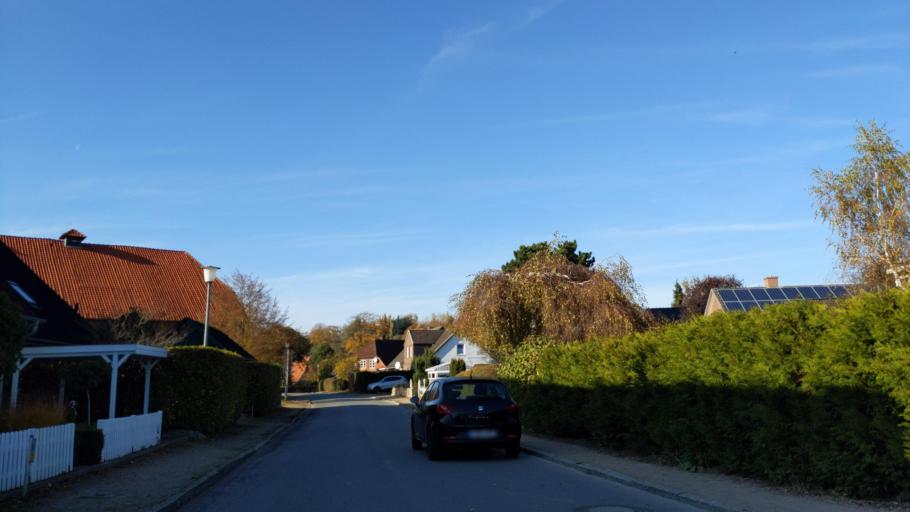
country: DE
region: Schleswig-Holstein
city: Eutin
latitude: 54.1538
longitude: 10.6250
